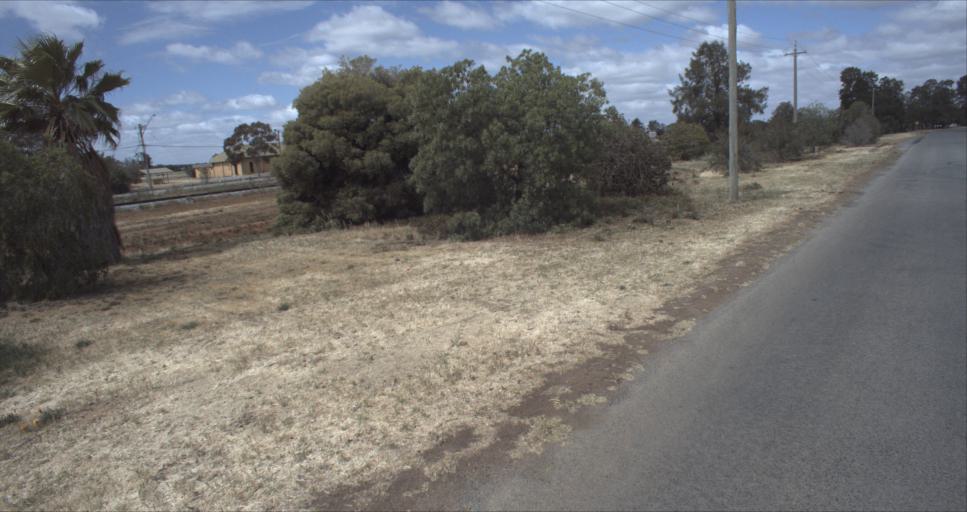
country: AU
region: New South Wales
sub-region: Leeton
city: Leeton
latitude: -34.5628
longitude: 146.3988
